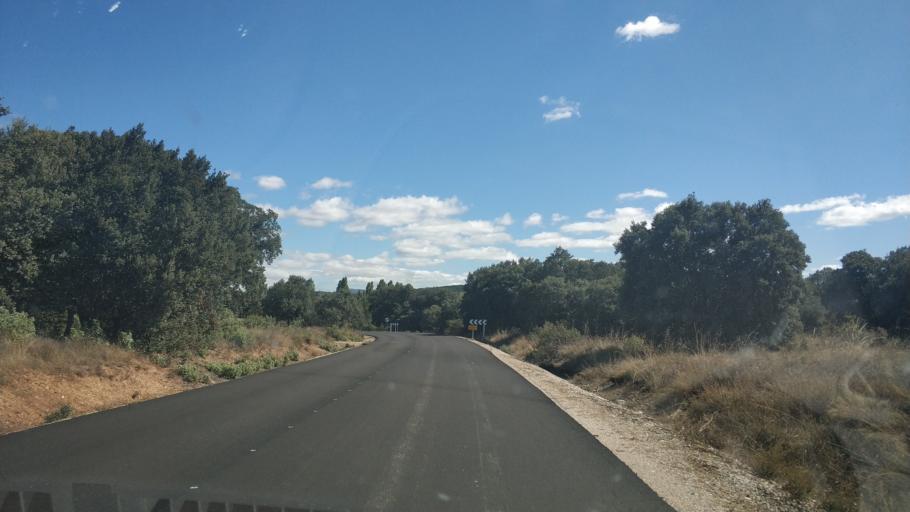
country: ES
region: Castille and Leon
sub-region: Provincia de Burgos
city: Puentedura
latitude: 42.0335
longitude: -3.6200
